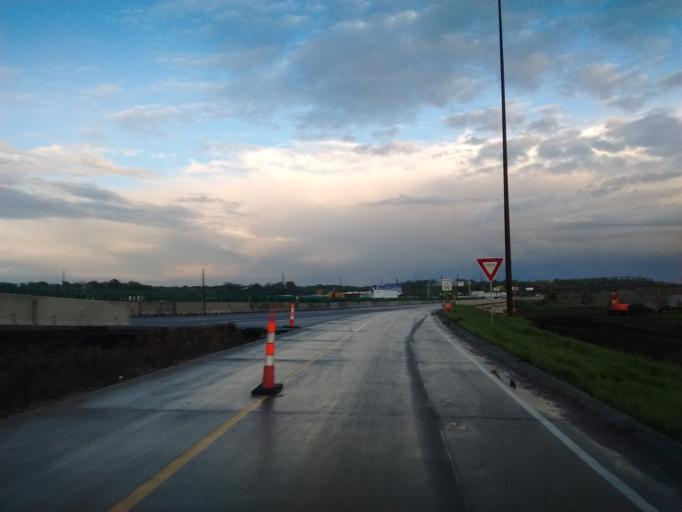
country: US
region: Iowa
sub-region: Woodbury County
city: Sioux City
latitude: 42.4851
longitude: -96.3933
